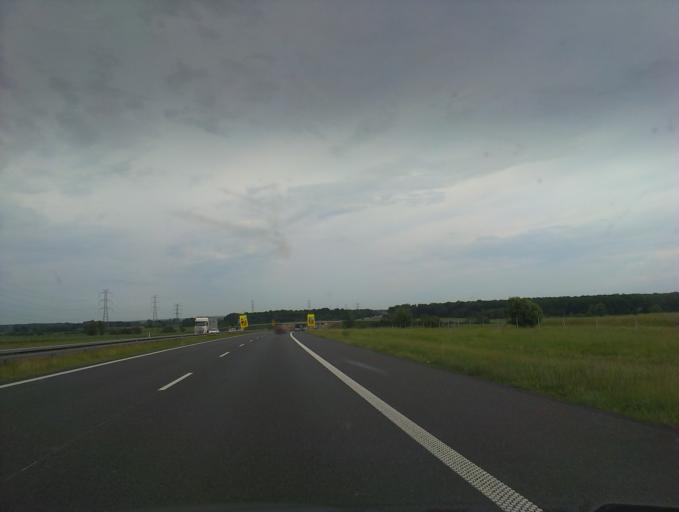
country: PL
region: Opole Voivodeship
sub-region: Powiat brzeski
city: Olszanka
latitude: 50.7351
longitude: 17.4927
